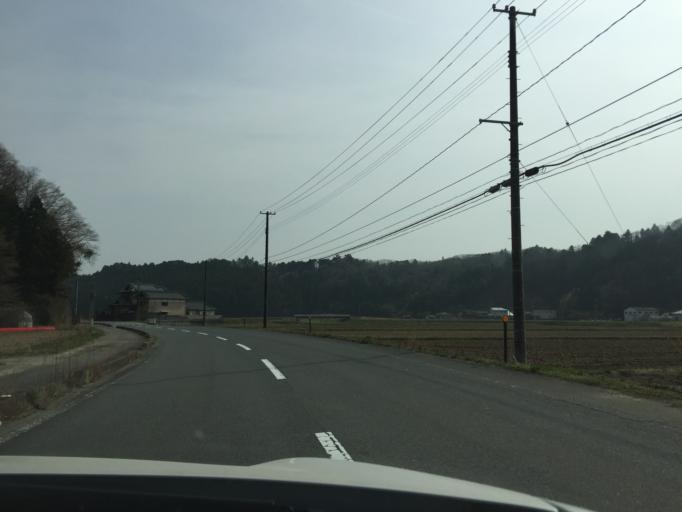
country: JP
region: Fukushima
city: Iwaki
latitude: 36.9728
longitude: 140.8018
